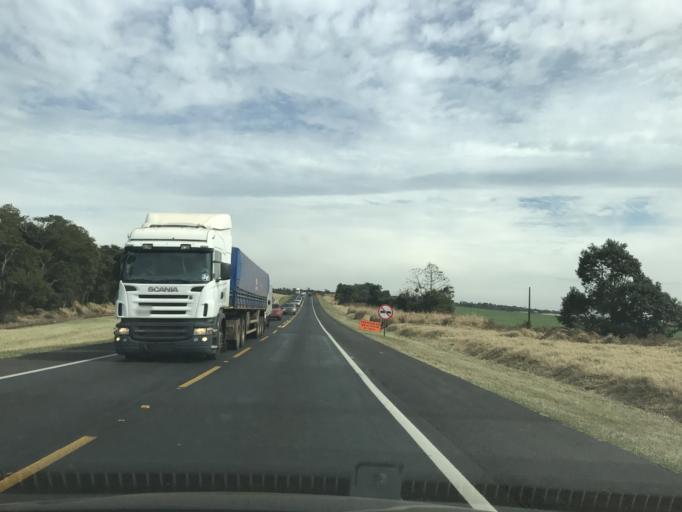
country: BR
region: Parana
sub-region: Cascavel
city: Cascavel
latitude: -25.0705
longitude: -53.6623
